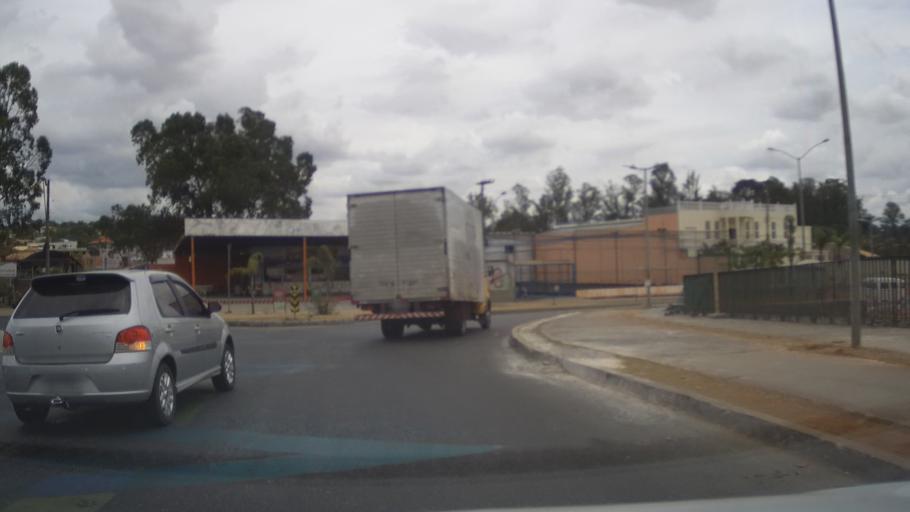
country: BR
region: Minas Gerais
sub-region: Belo Horizonte
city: Belo Horizonte
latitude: -19.8608
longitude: -43.9972
